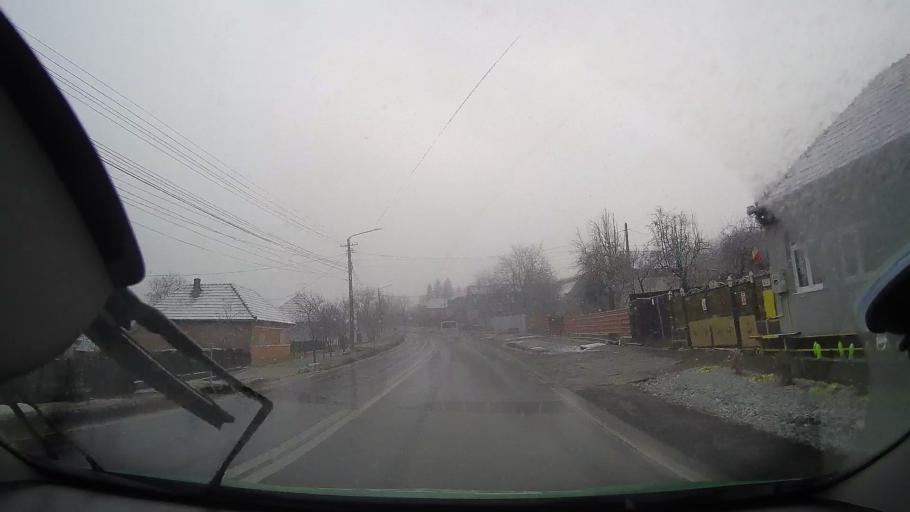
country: RO
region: Mures
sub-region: Comuna Bagaciu
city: Delenii
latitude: 46.2777
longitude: 24.3007
